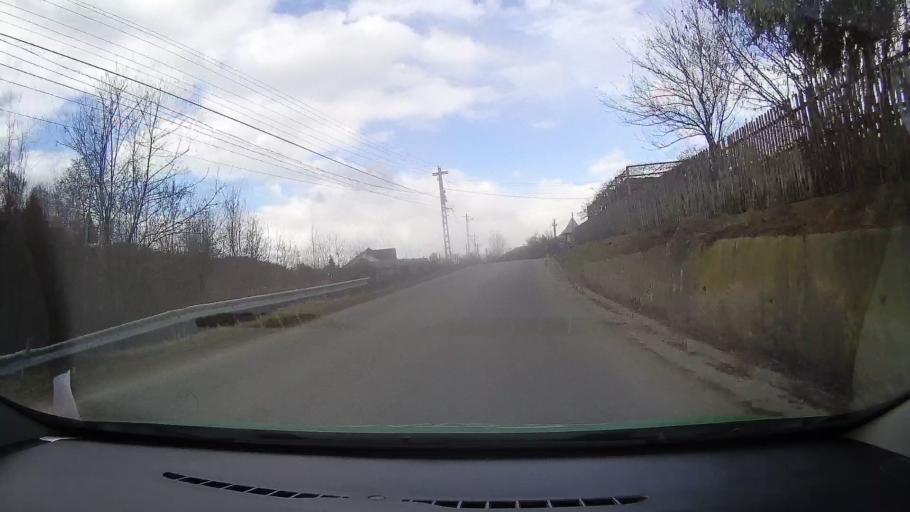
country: RO
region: Dambovita
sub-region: Comuna Visinesti
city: Visinesti
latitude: 45.0741
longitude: 25.5411
